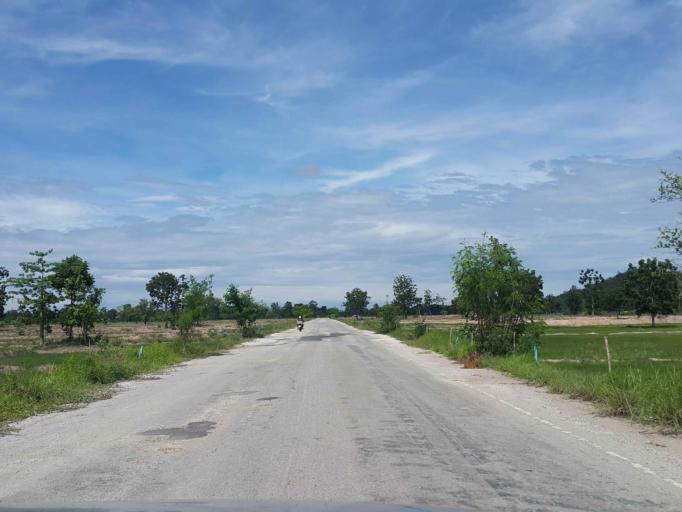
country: TH
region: Sukhothai
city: Ban Dan Lan Hoi
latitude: 17.1106
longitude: 99.4922
